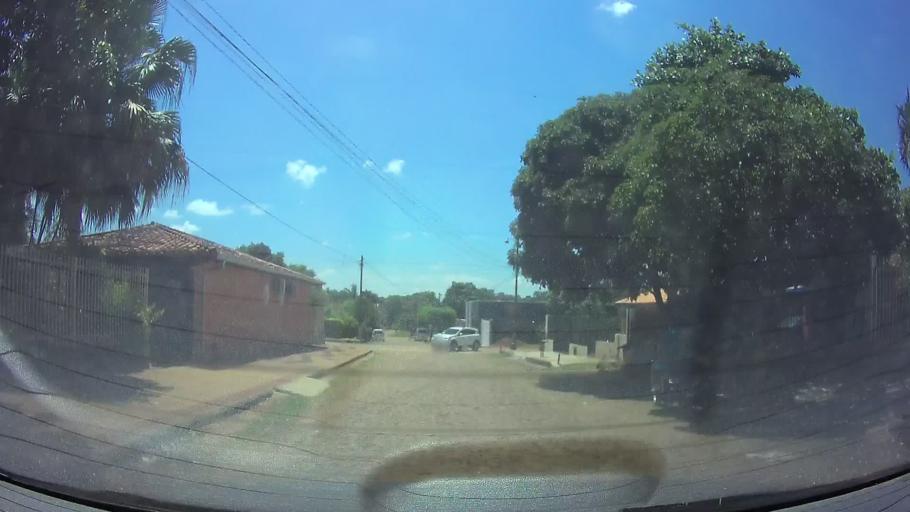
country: PY
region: Central
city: San Lorenzo
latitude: -25.2615
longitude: -57.4858
